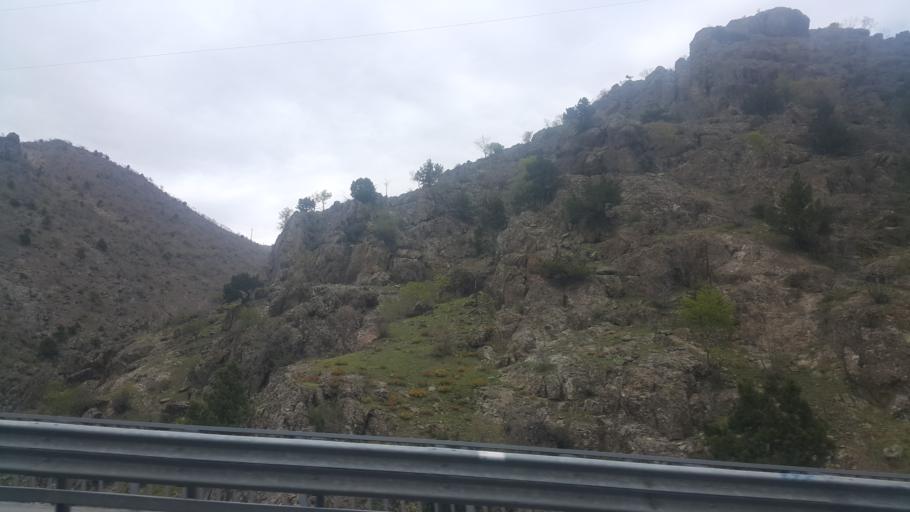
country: TR
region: Nigde
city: Ciftehan
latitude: 37.5534
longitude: 34.7742
